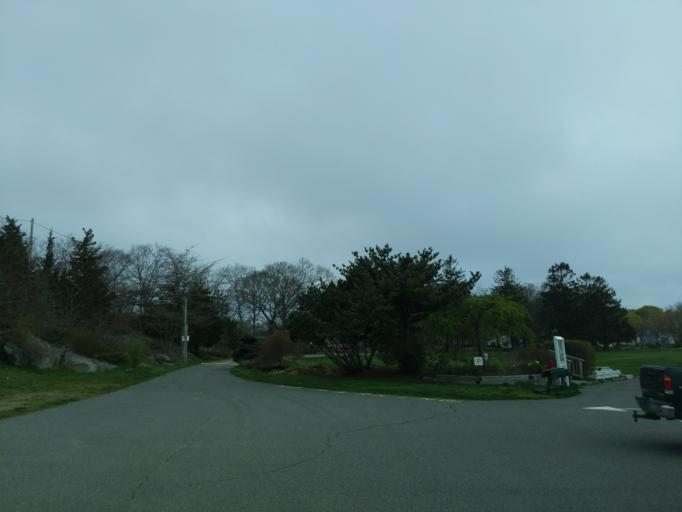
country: US
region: Massachusetts
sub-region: Essex County
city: Rockport
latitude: 42.6506
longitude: -70.6059
